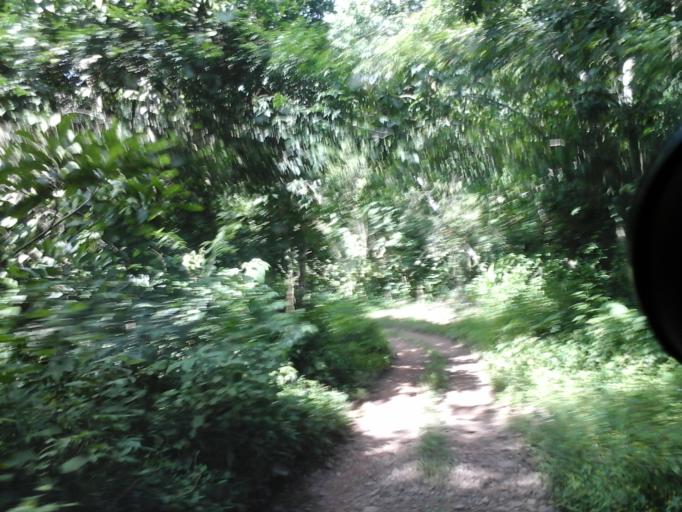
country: CO
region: Cesar
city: San Diego
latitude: 10.2741
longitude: -73.0928
